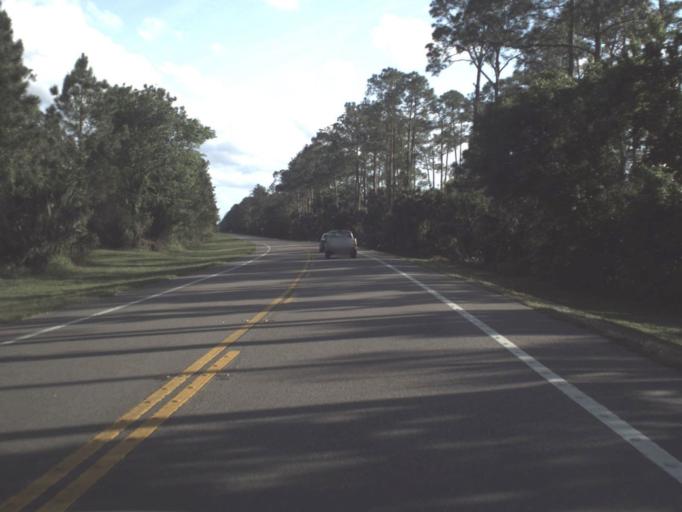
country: US
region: Florida
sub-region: Flagler County
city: Bunnell
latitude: 29.4145
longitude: -81.3045
